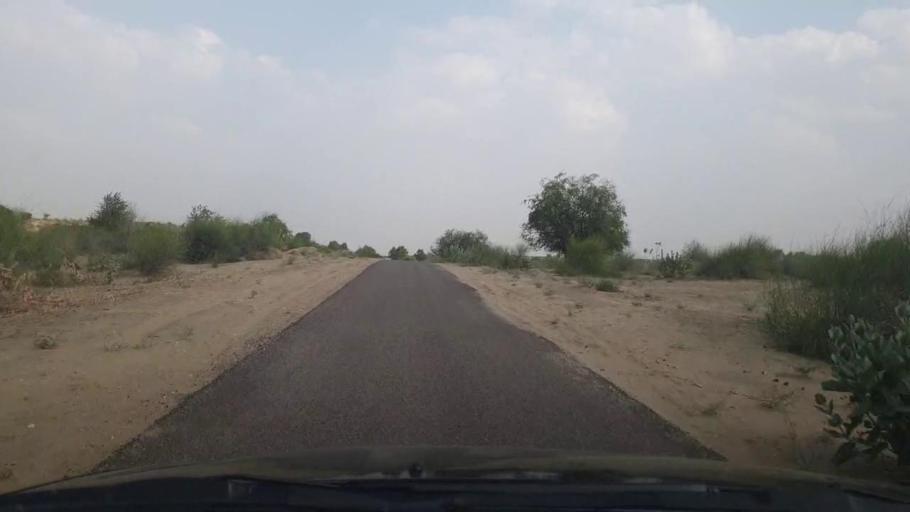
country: PK
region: Sindh
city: Islamkot
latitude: 25.0065
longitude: 70.6558
